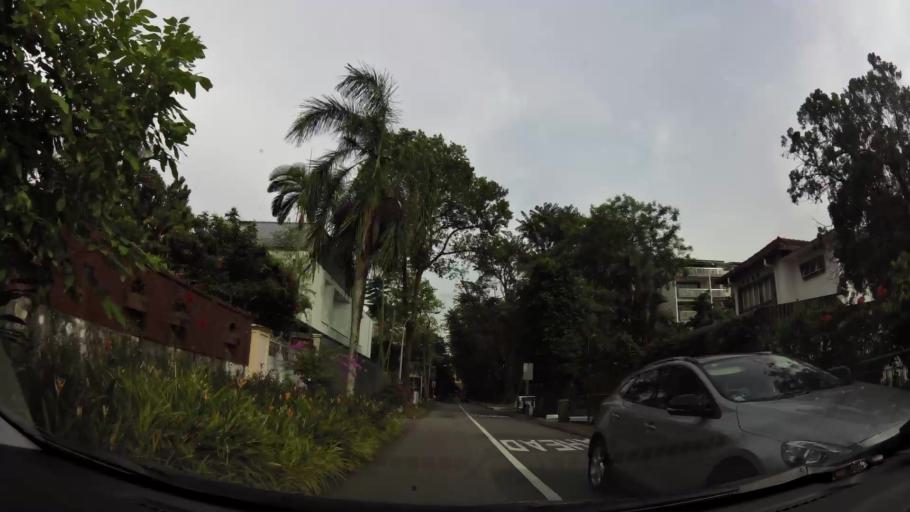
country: SG
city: Singapore
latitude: 1.3230
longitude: 103.8222
